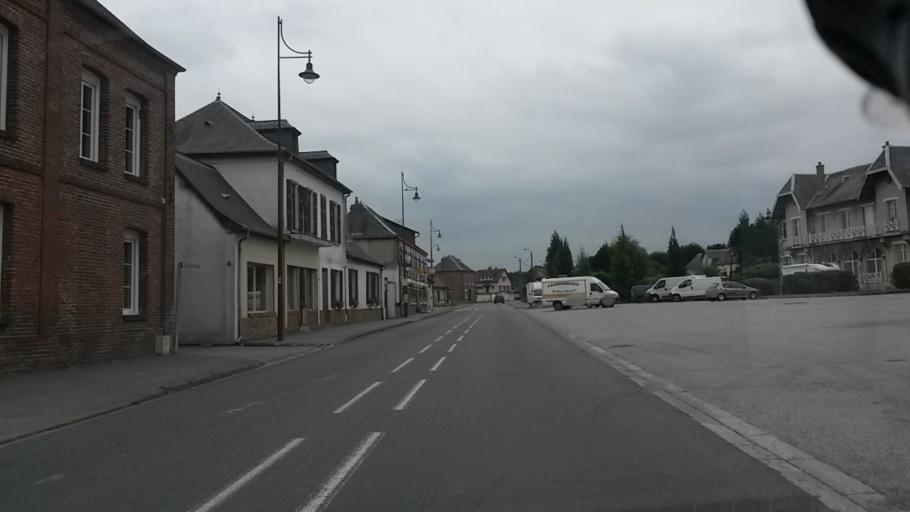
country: FR
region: Picardie
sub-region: Departement de la Somme
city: Hornoy-le-Bourg
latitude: 49.7751
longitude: 1.8652
